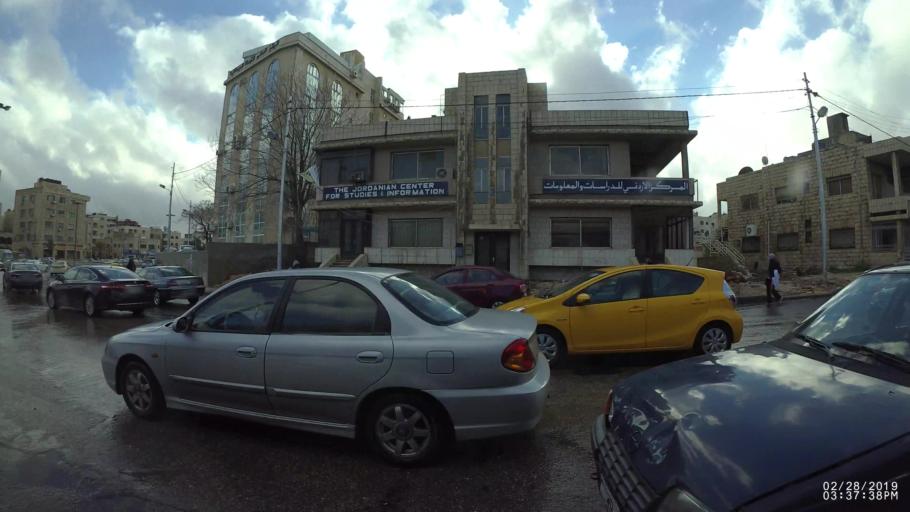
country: JO
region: Amman
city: Al Jubayhah
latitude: 31.9860
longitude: 35.8974
